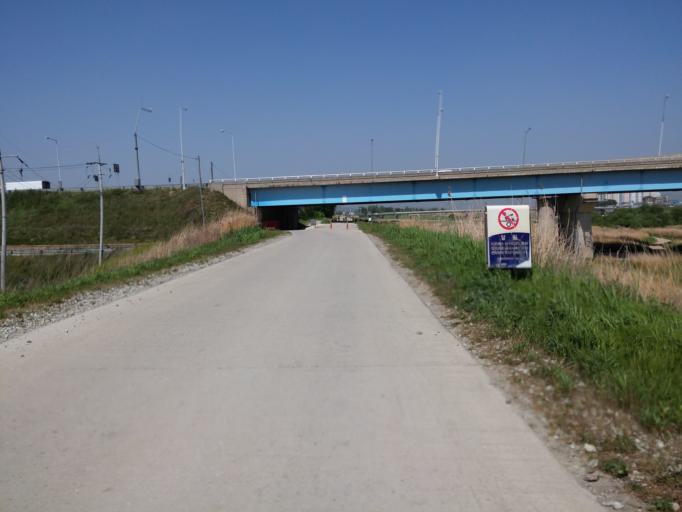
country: KR
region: Chungcheongnam-do
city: Nonsan
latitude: 36.2073
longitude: 127.0742
